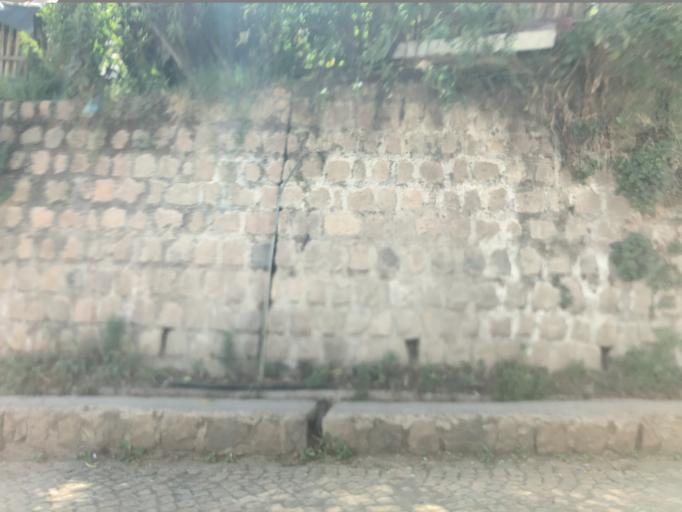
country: ET
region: Amhara
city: Lalibela
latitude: 12.0348
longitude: 39.0481
